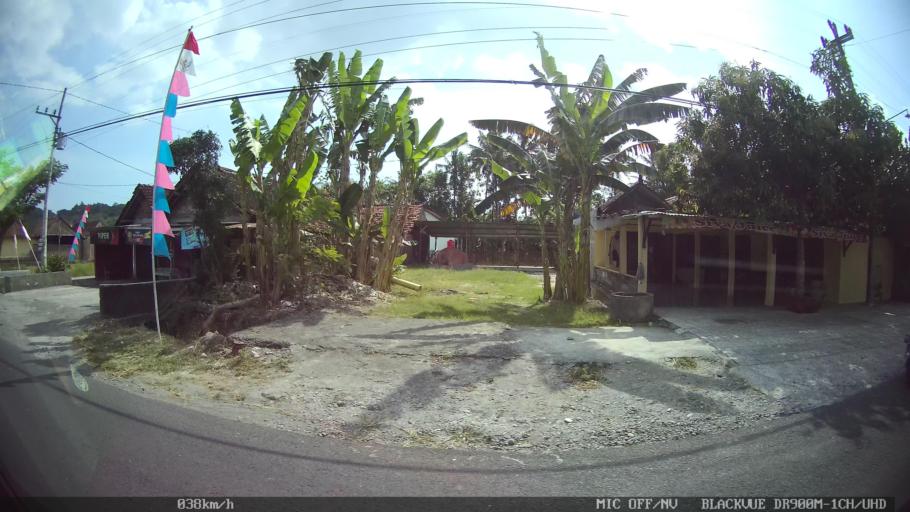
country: ID
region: Daerah Istimewa Yogyakarta
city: Kasihan
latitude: -7.8454
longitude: 110.3147
